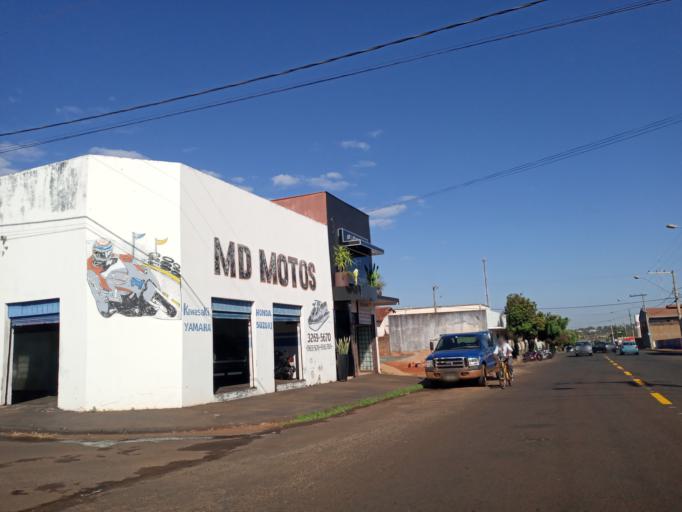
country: BR
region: Minas Gerais
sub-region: Ituiutaba
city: Ituiutaba
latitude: -18.9838
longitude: -49.4659
